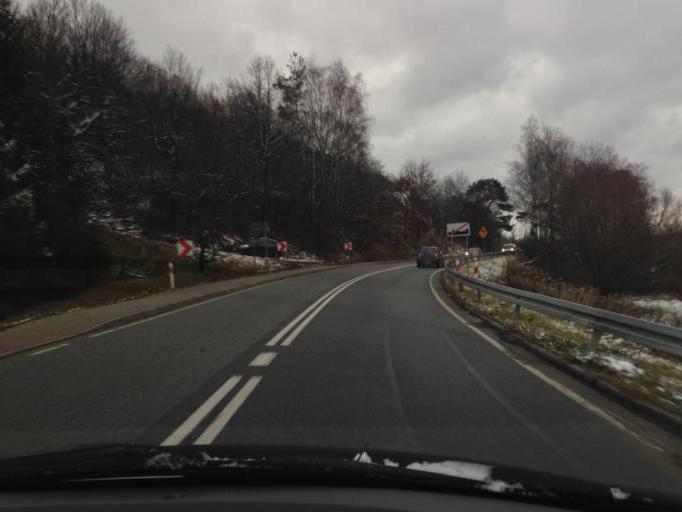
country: PL
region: Lesser Poland Voivodeship
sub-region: Powiat tarnowski
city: Zakliczyn
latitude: 49.8691
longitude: 20.7820
